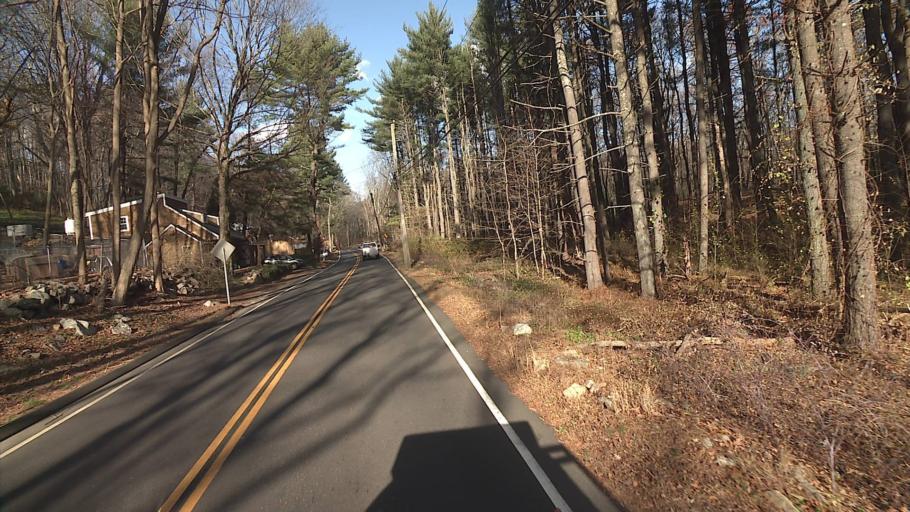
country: US
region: Connecticut
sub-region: Fairfield County
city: Georgetown
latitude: 41.2602
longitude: -73.3742
